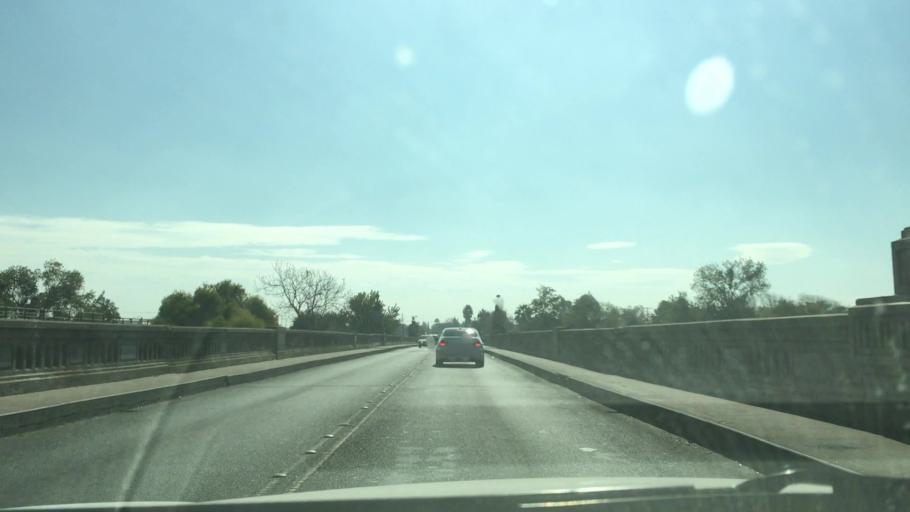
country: US
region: California
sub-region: Stanislaus County
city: Bystrom
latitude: 37.6277
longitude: -120.9937
